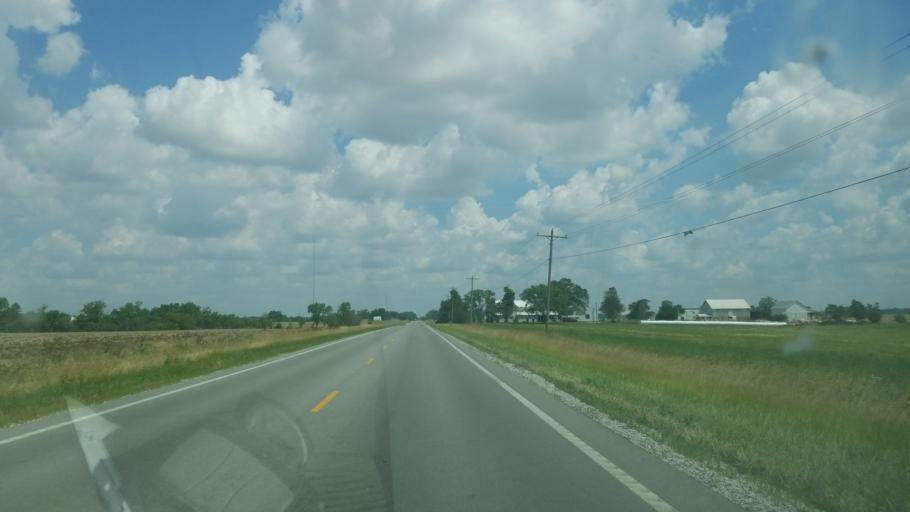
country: US
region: Ohio
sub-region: Auglaize County
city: Wapakoneta
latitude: 40.6091
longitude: -84.2030
